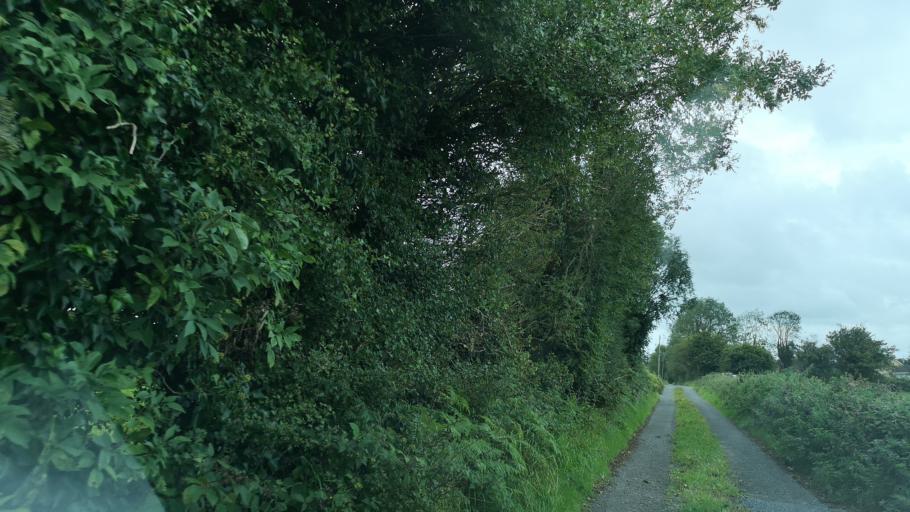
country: IE
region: Connaught
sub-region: County Galway
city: Athenry
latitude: 53.3300
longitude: -8.7579
